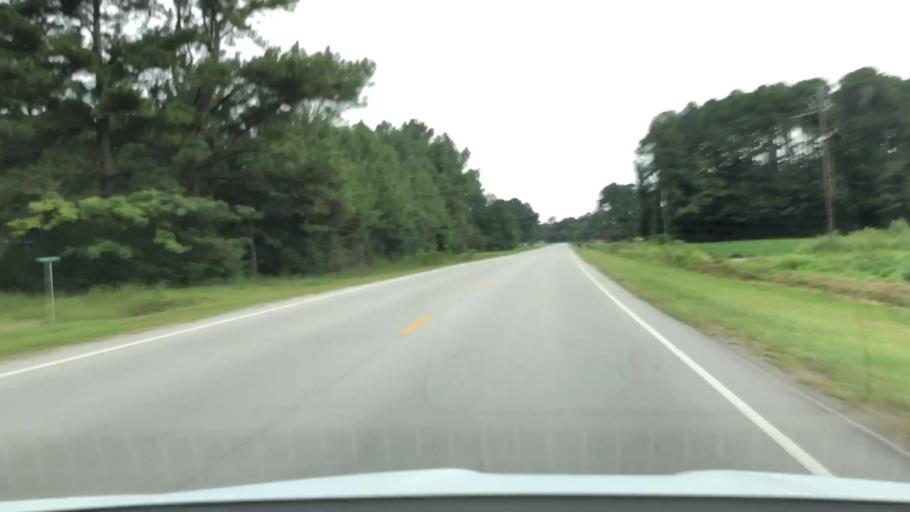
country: US
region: North Carolina
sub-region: Jones County
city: Trenton
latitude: 35.0219
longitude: -77.3047
